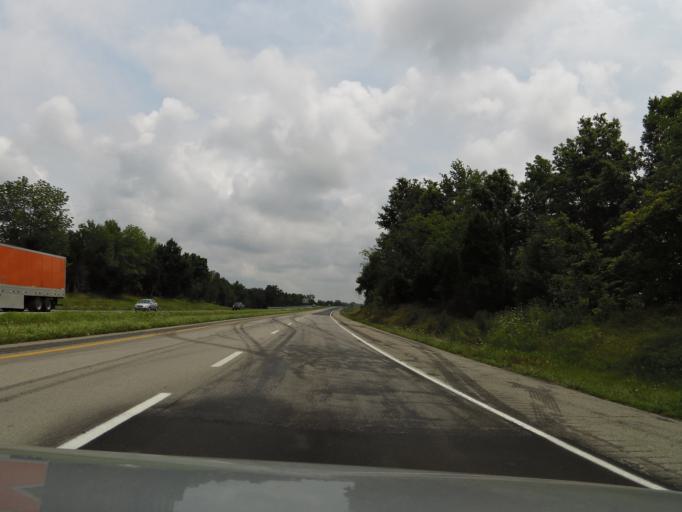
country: US
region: Kentucky
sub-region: Grayson County
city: Leitchfield
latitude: 37.4914
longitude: -86.2023
